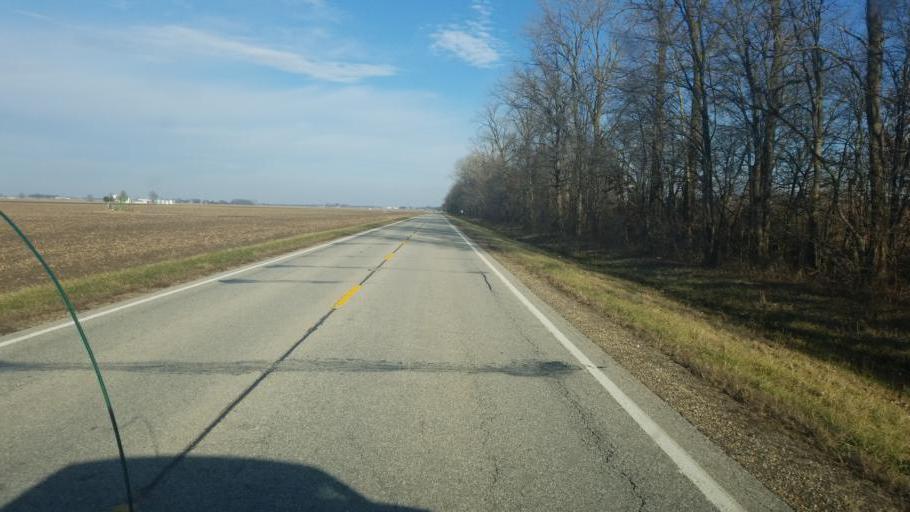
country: US
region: Illinois
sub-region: Edwards County
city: Grayville
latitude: 38.3244
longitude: -87.9150
